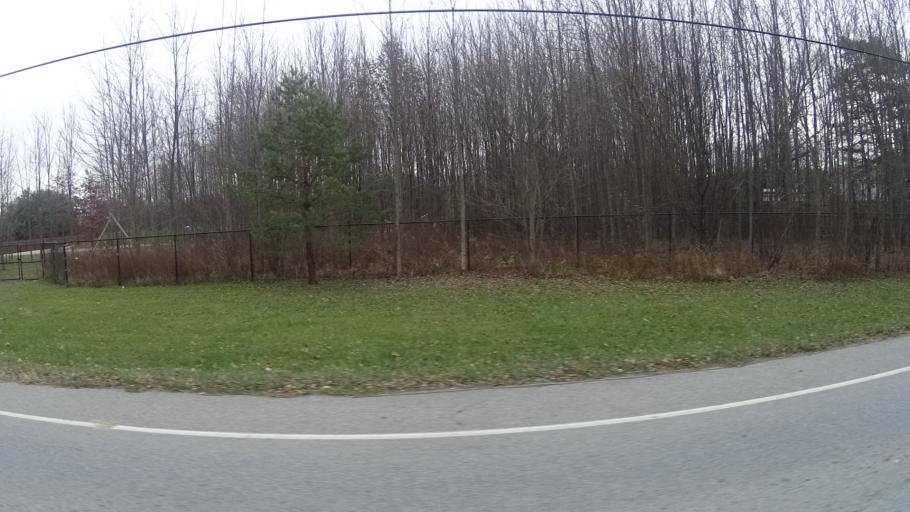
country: US
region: Ohio
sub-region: Cuyahoga County
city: Olmsted Falls
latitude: 41.3367
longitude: -81.9431
